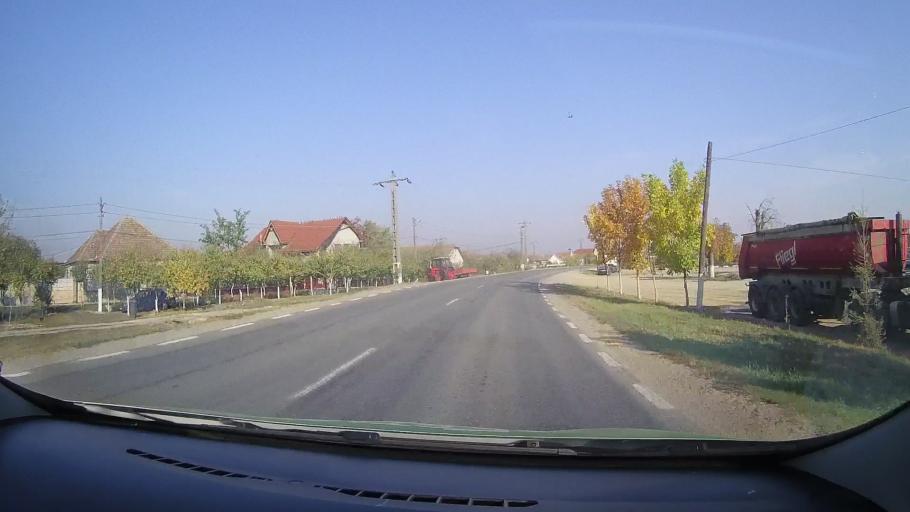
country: RO
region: Arad
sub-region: Comuna Pilu
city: Pilu
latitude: 46.5705
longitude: 21.3423
